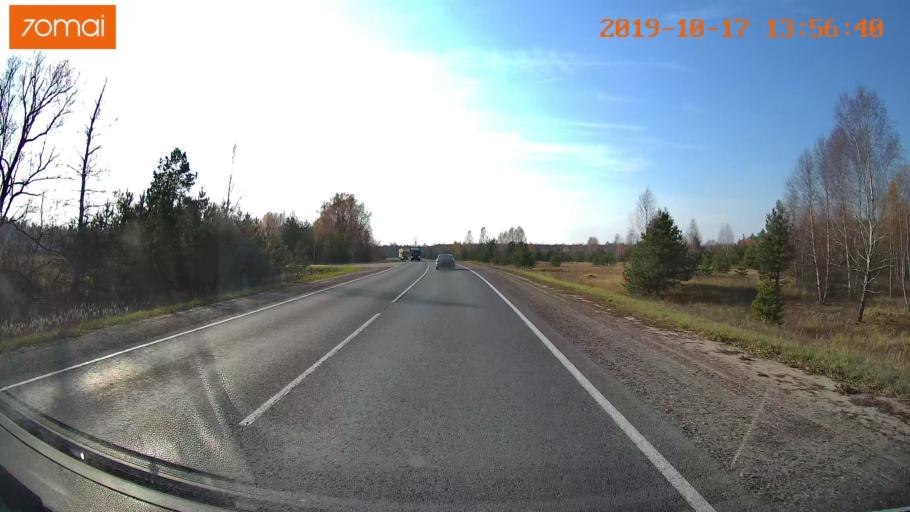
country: RU
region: Rjazan
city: Spas-Klepiki
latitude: 55.1500
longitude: 40.2613
